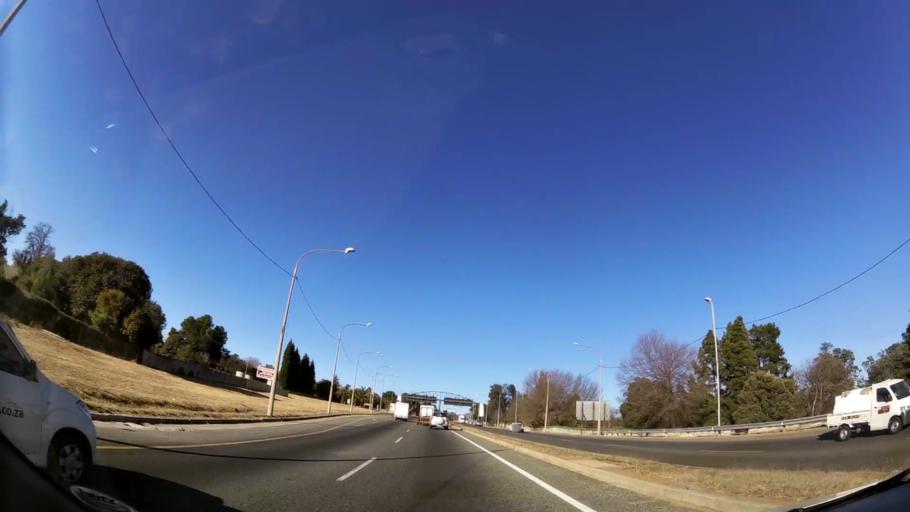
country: ZA
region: Gauteng
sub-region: West Rand District Municipality
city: Krugersdorp
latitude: -26.0811
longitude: 27.7896
